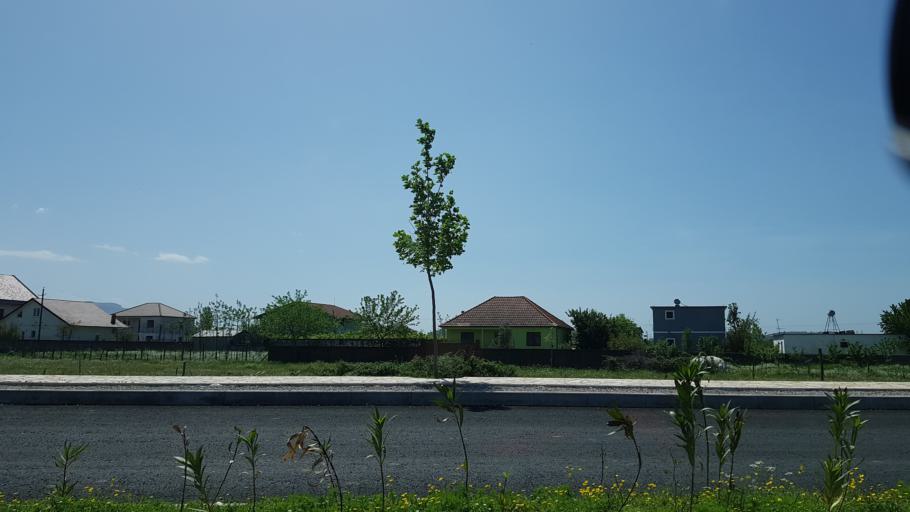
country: AL
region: Shkoder
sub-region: Rrethi i Shkodres
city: Shkoder
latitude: 42.0847
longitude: 19.5024
